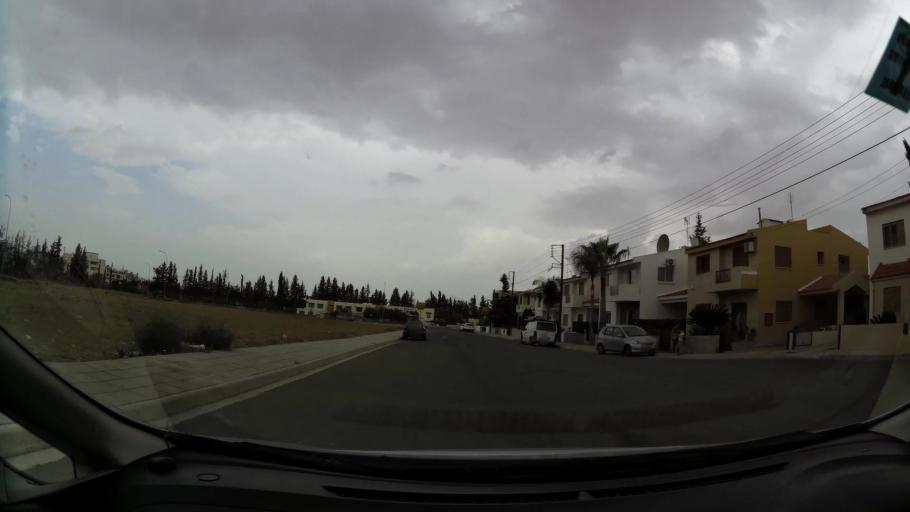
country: CY
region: Lefkosia
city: Geri
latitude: 35.0948
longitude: 33.3810
